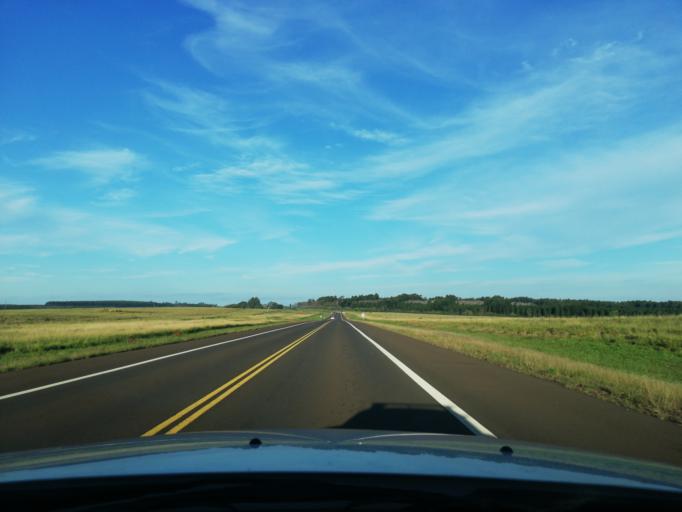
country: AR
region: Misiones
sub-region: Departamento de Capital
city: Posadas
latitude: -27.4546
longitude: -56.0171
